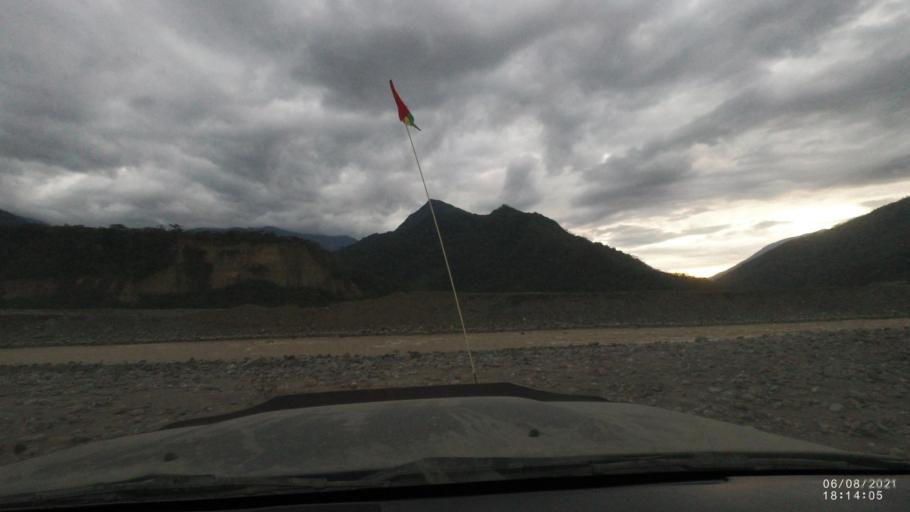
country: BO
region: La Paz
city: Quime
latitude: -16.4712
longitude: -66.7864
